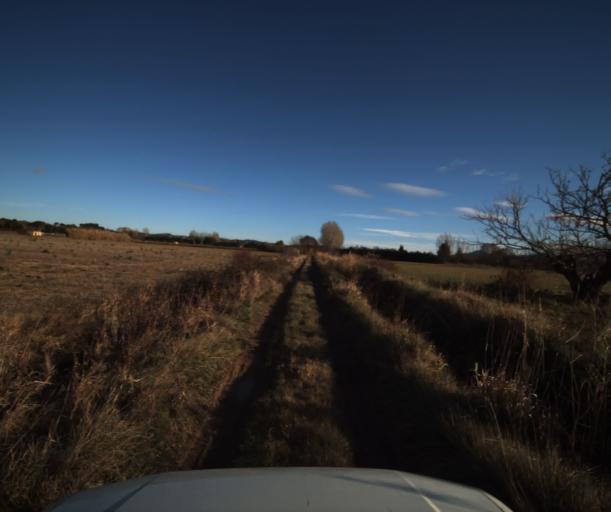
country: FR
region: Provence-Alpes-Cote d'Azur
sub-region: Departement du Vaucluse
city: Pertuis
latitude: 43.6927
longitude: 5.4682
